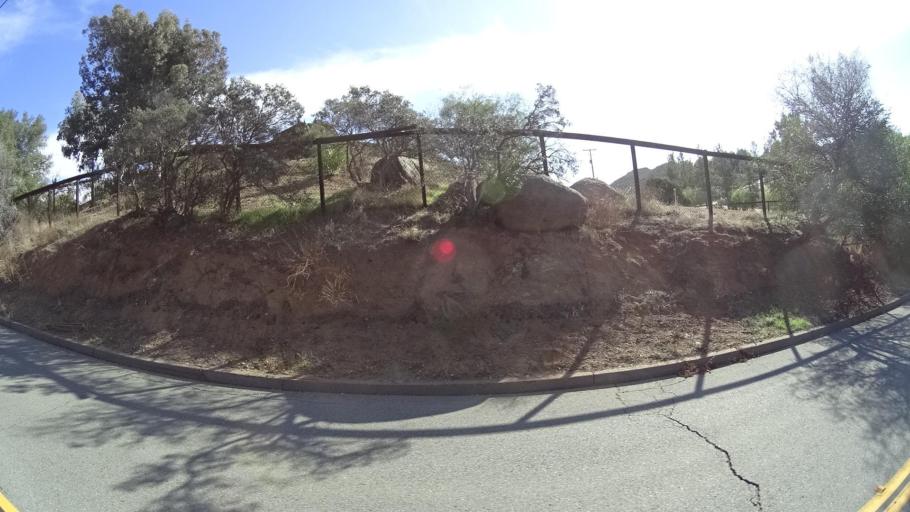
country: US
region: California
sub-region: San Diego County
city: Alpine
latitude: 32.8141
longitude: -116.7464
